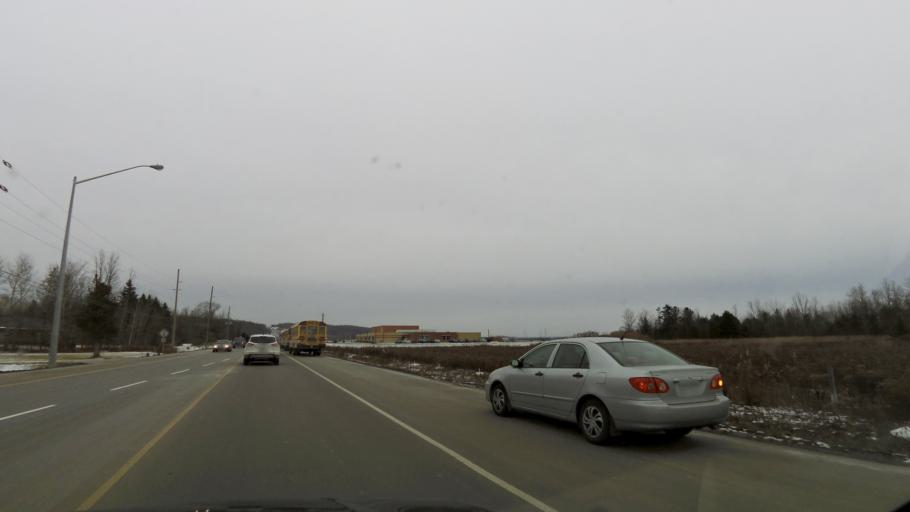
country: CA
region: Ontario
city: Newmarket
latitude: 44.1032
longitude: -79.5199
